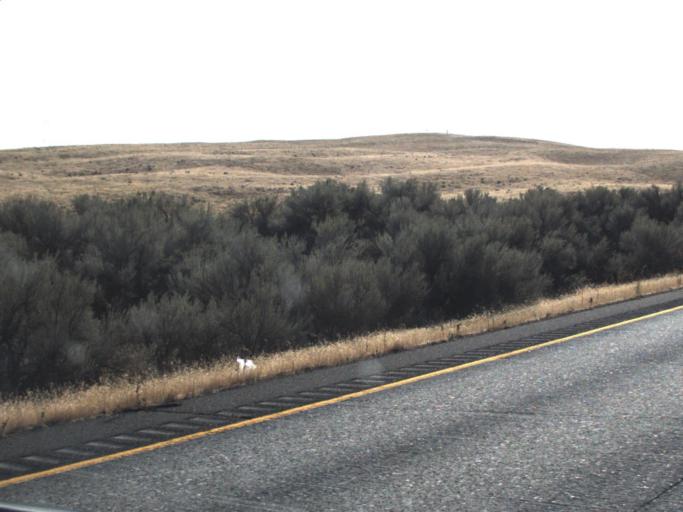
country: US
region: Oregon
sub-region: Umatilla County
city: Umatilla
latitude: 45.9943
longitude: -119.2820
